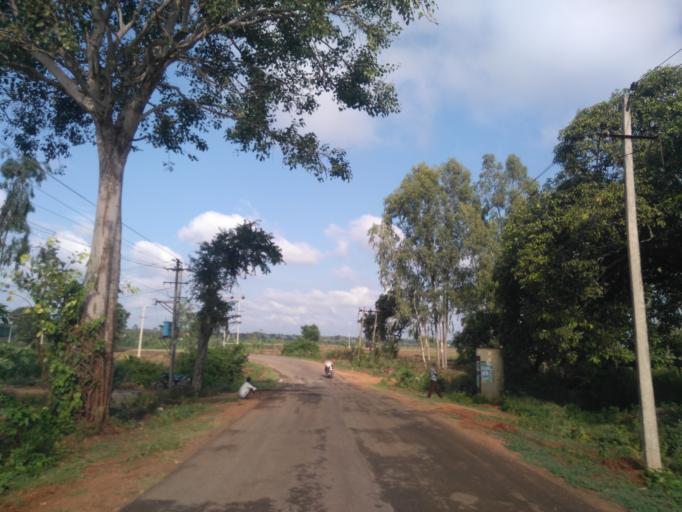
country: IN
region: Karnataka
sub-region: Mysore
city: Tirumakudal Narsipur
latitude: 12.2586
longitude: 76.9950
